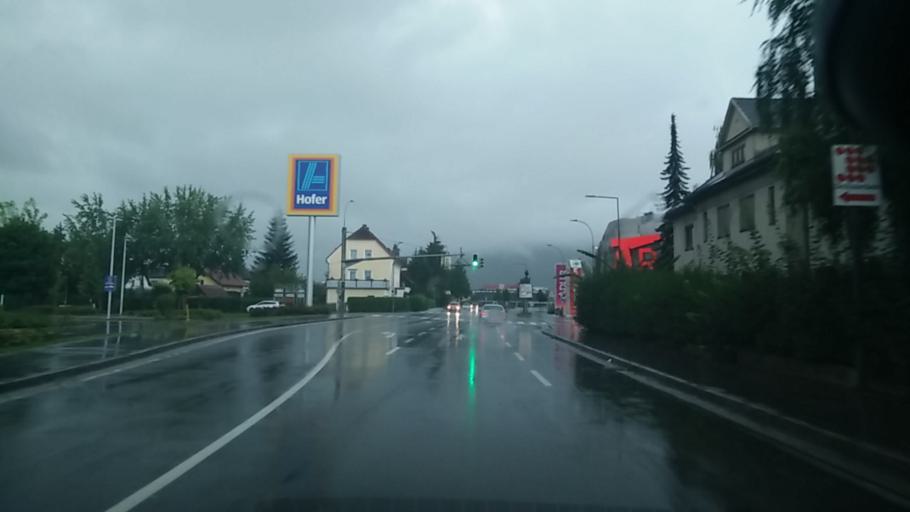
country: AT
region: Carinthia
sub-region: Villach Stadt
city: Villach
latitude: 46.5973
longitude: 13.8384
